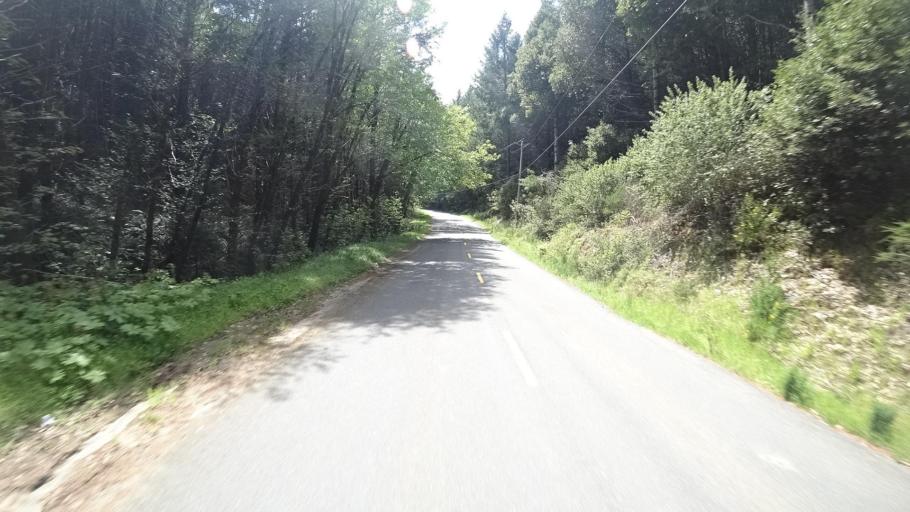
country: US
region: California
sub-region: Humboldt County
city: Redway
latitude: 40.0824
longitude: -123.9509
